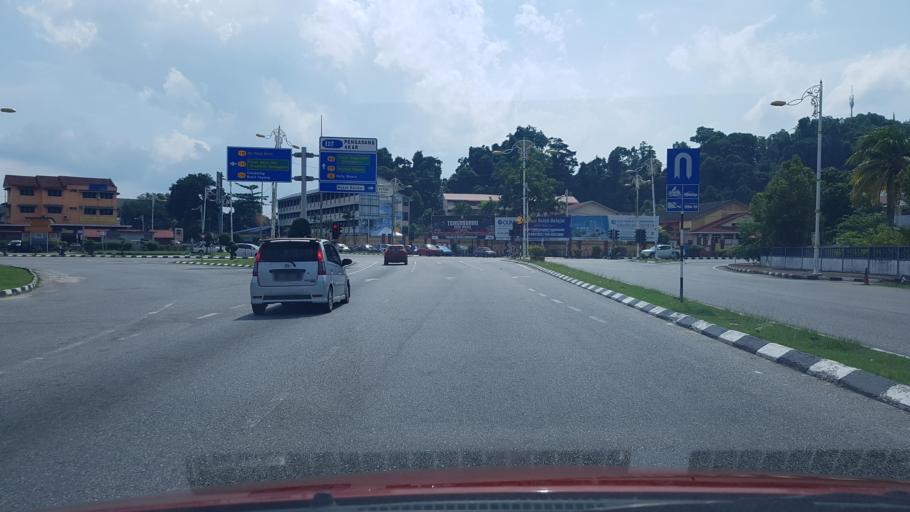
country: MY
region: Terengganu
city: Kuala Terengganu
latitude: 5.3145
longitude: 103.1454
